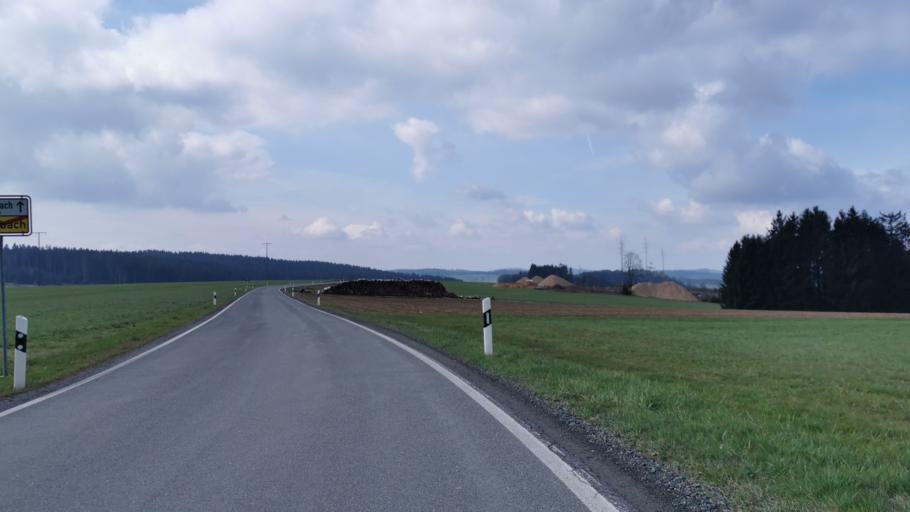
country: DE
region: Bavaria
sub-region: Upper Franconia
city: Tettau
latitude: 50.4421
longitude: 11.3124
